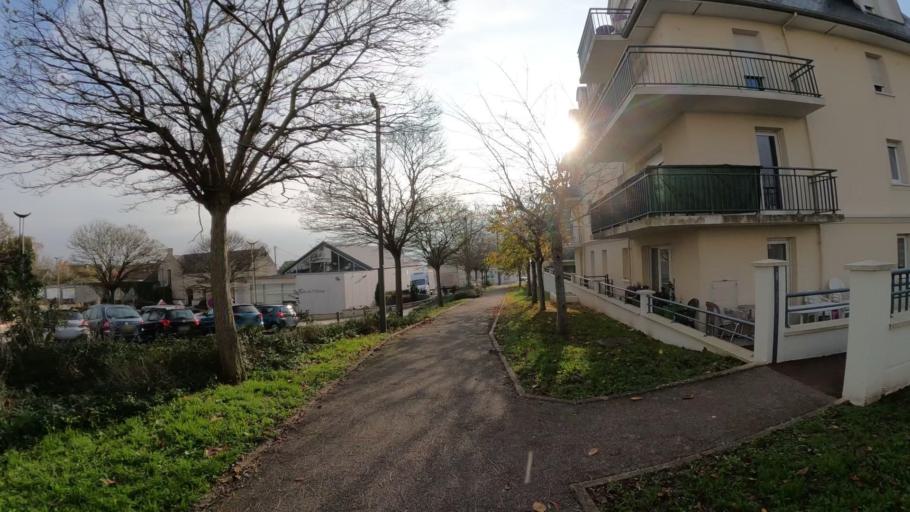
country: FR
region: Lower Normandy
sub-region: Departement du Calvados
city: Saint-Germain-la-Blanche-Herbe
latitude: 49.1889
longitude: -0.4105
